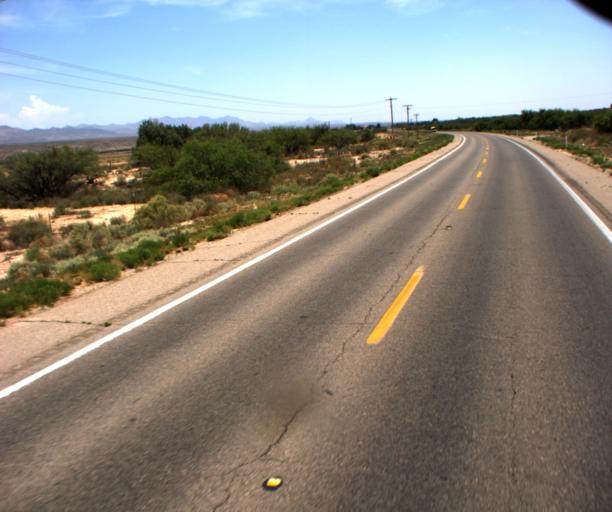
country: US
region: Arizona
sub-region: Graham County
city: Bylas
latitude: 33.0425
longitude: -109.9792
